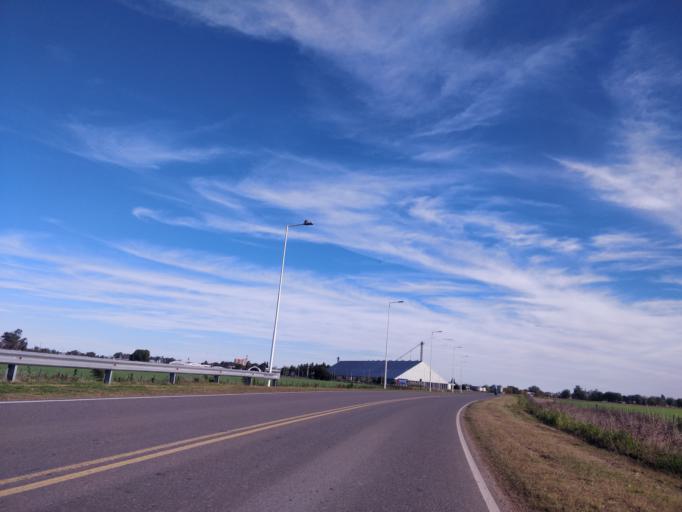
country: AR
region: Cordoba
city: Leones
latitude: -32.6473
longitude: -62.2919
